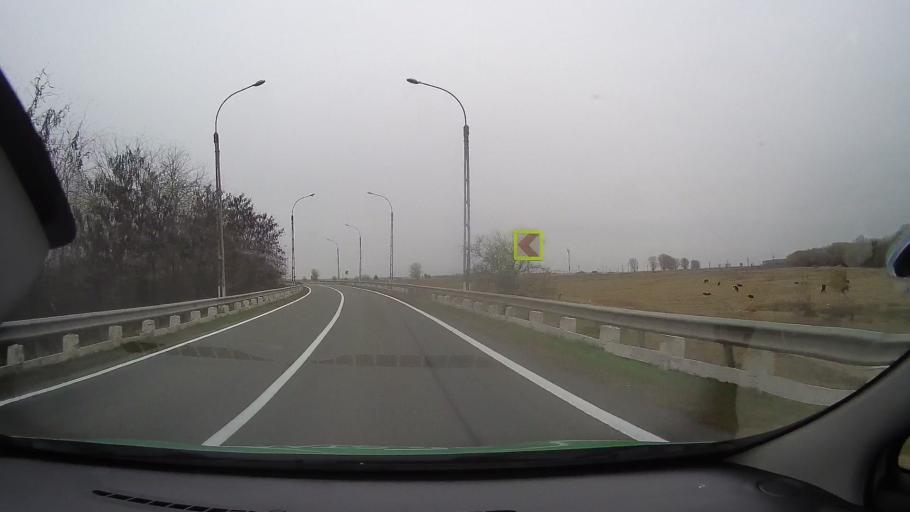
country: RO
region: Ialomita
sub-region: Comuna Giurgeni
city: Giurgeni
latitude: 44.7558
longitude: 27.8615
